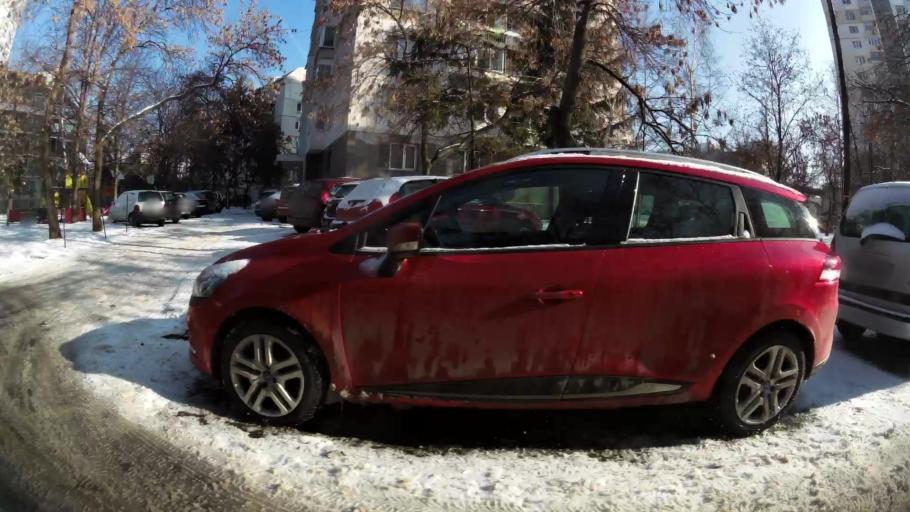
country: BG
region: Sofia-Capital
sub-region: Stolichna Obshtina
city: Sofia
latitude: 42.6592
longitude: 23.3402
